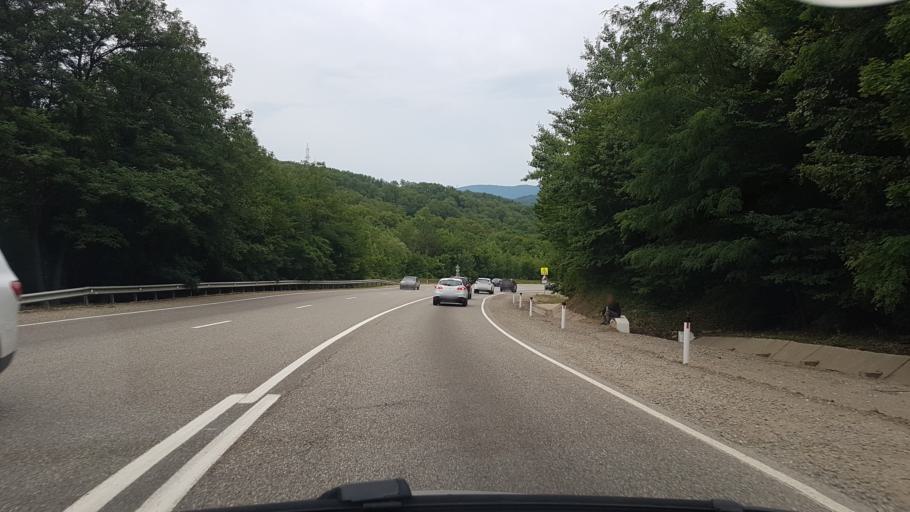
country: RU
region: Krasnodarskiy
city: Novomikhaylovskiy
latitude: 44.4852
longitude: 38.8999
